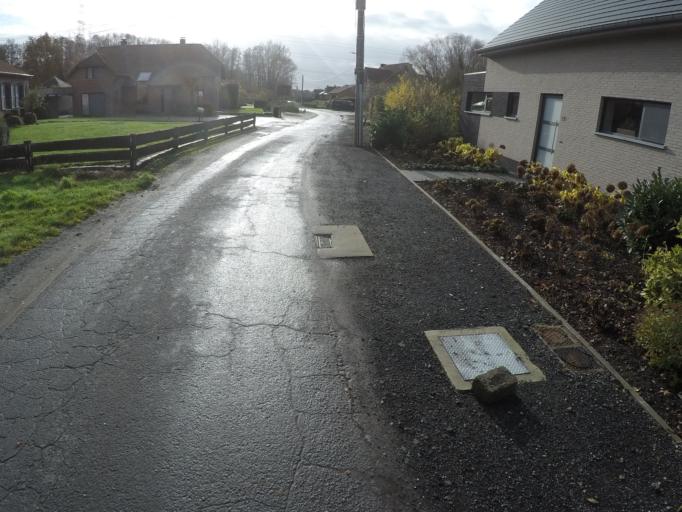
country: BE
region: Flanders
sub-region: Provincie Vlaams-Brabant
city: Londerzeel
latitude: 51.0250
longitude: 4.3039
